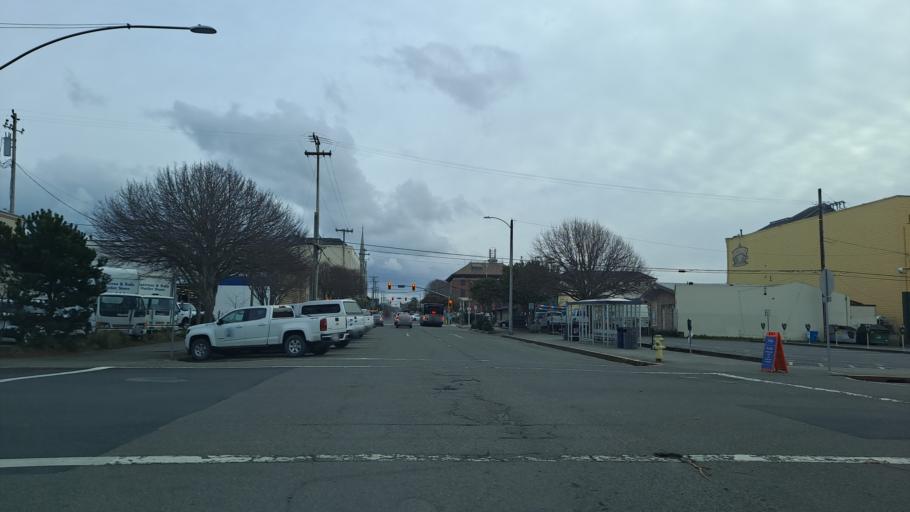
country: US
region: California
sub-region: Humboldt County
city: Eureka
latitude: 40.8040
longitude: -124.1642
